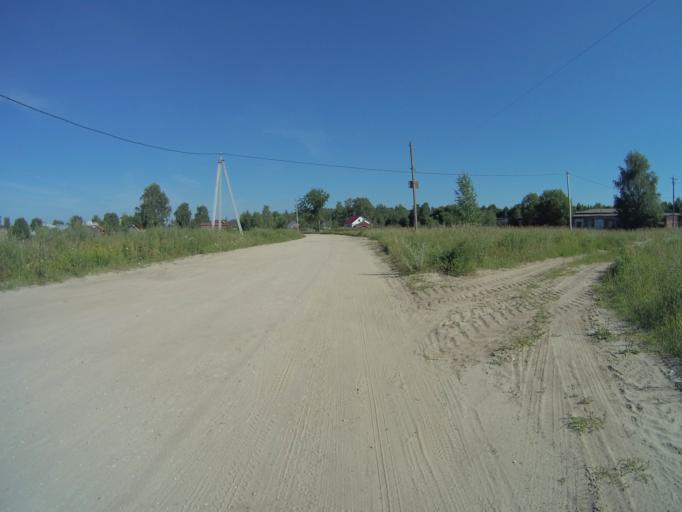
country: RU
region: Vladimir
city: Raduzhnyy
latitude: 56.0261
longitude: 40.3093
